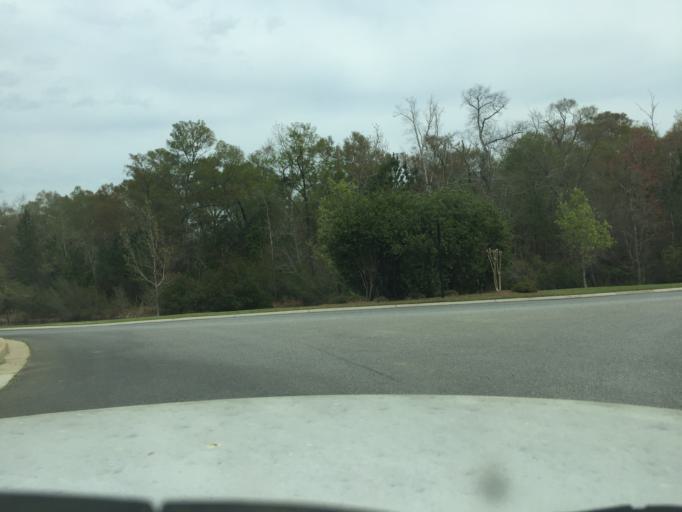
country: US
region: Georgia
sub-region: Chatham County
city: Georgetown
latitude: 32.0490
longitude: -81.2395
